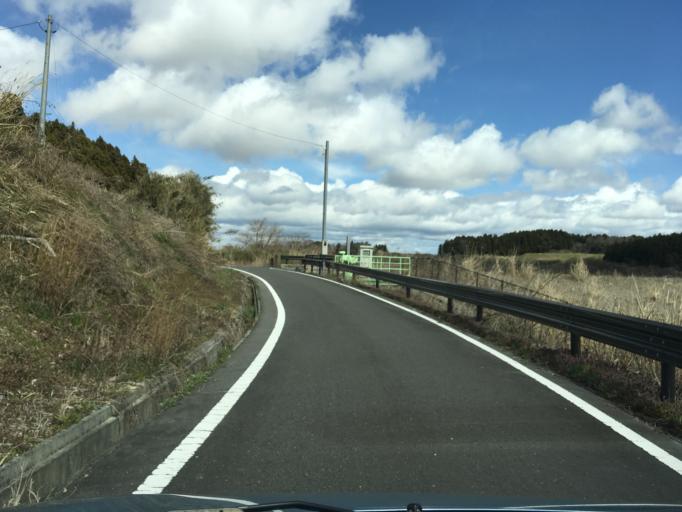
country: JP
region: Miyagi
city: Wakuya
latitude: 38.6838
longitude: 141.1038
